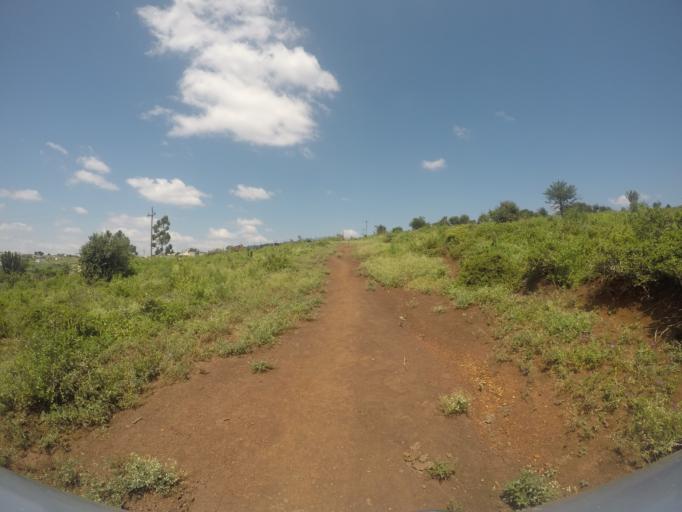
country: ZA
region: KwaZulu-Natal
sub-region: uThungulu District Municipality
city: Empangeni
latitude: -28.6024
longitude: 31.7363
